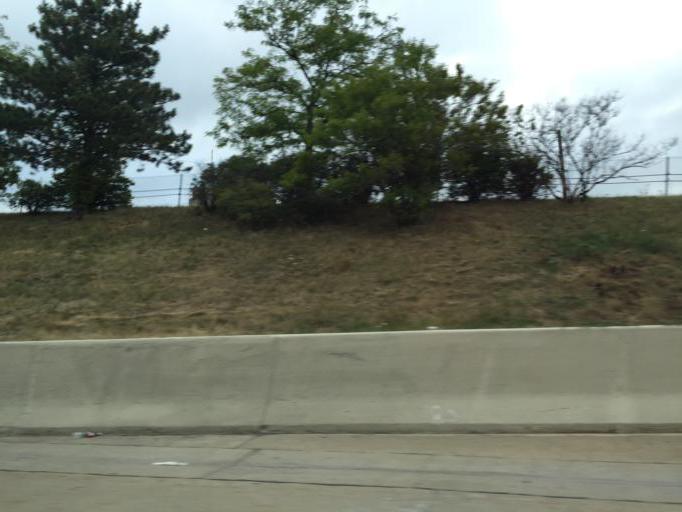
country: US
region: Michigan
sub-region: Wayne County
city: Hamtramck
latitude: 42.3656
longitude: -83.0805
